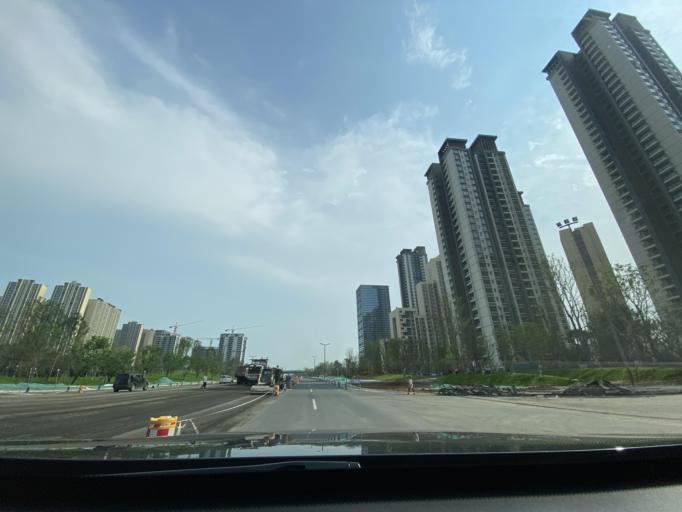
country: CN
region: Sichuan
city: Longquan
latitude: 30.4191
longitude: 104.1014
